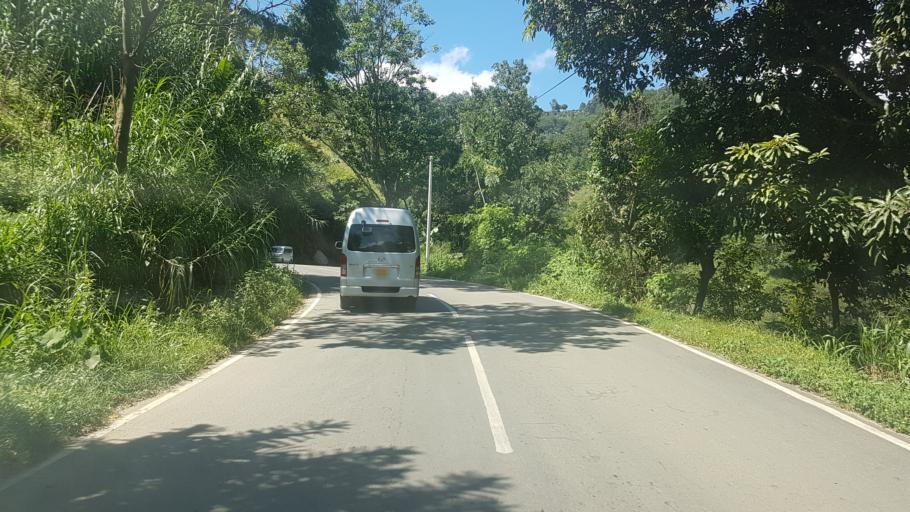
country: LK
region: Uva
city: Badulla
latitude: 6.8671
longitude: 81.0502
